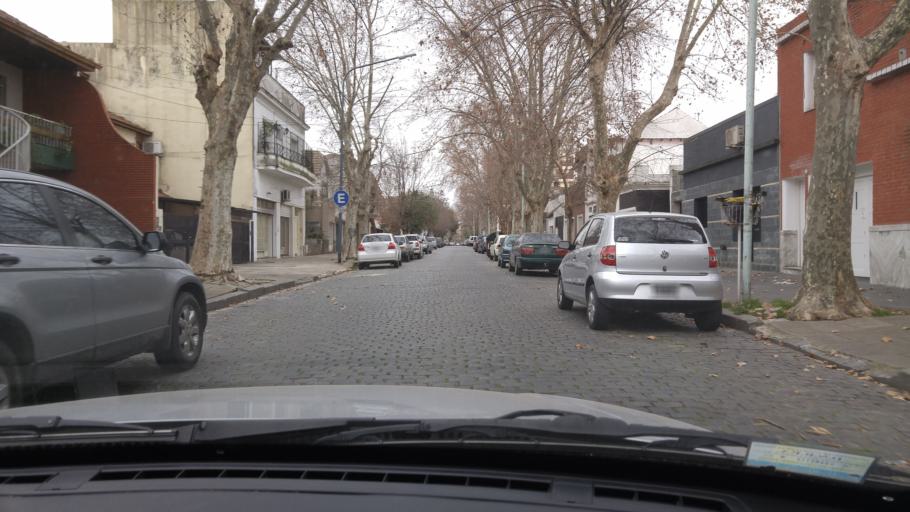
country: AR
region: Buenos Aires F.D.
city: Villa Santa Rita
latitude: -34.6300
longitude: -58.5255
